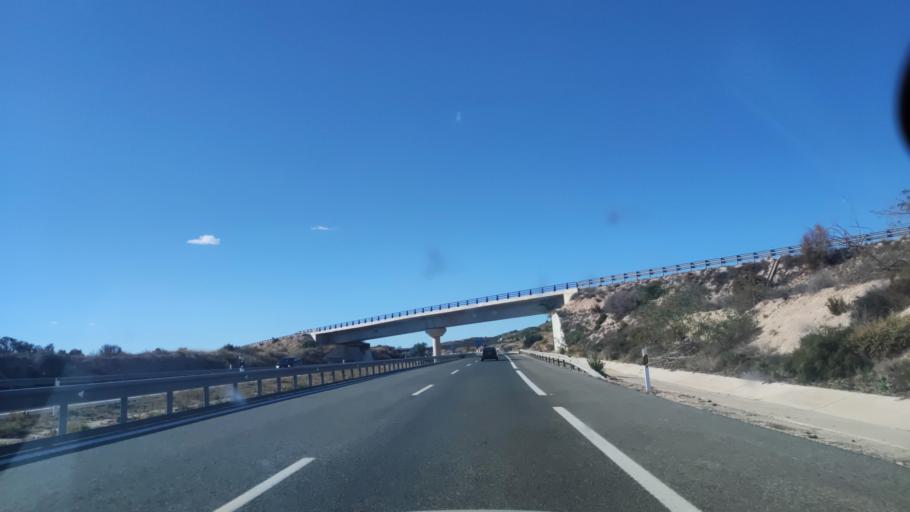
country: ES
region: Valencia
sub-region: Provincia de Alicante
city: el Campello
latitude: 38.4479
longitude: -0.3845
